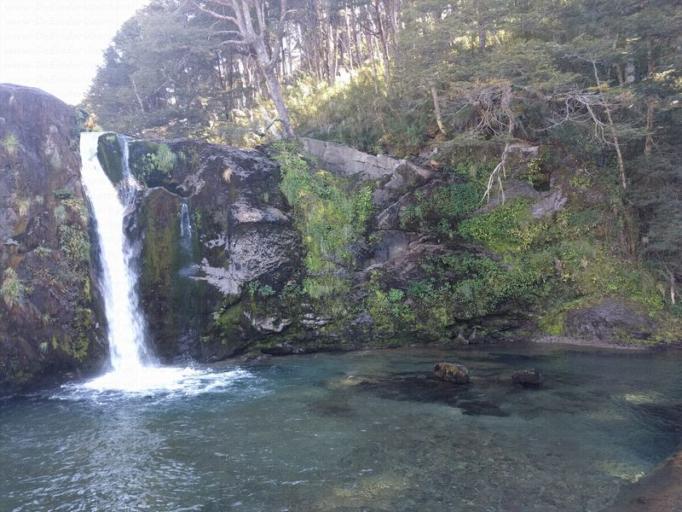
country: AR
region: Neuquen
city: Villa La Angostura
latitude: -40.4876
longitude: -71.6634
